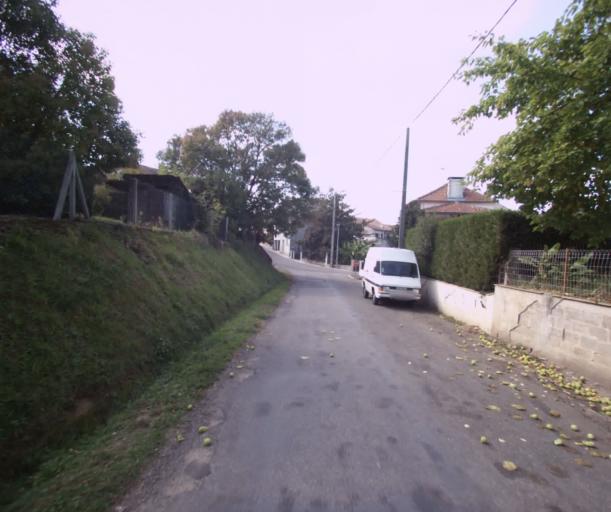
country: FR
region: Midi-Pyrenees
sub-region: Departement du Gers
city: Cazaubon
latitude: 43.9352
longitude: -0.0712
